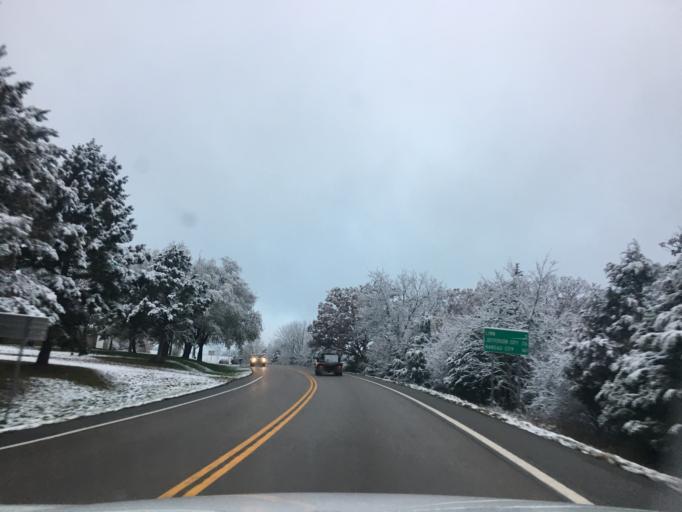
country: US
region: Missouri
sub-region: Osage County
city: Linn
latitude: 38.4751
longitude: -91.7855
